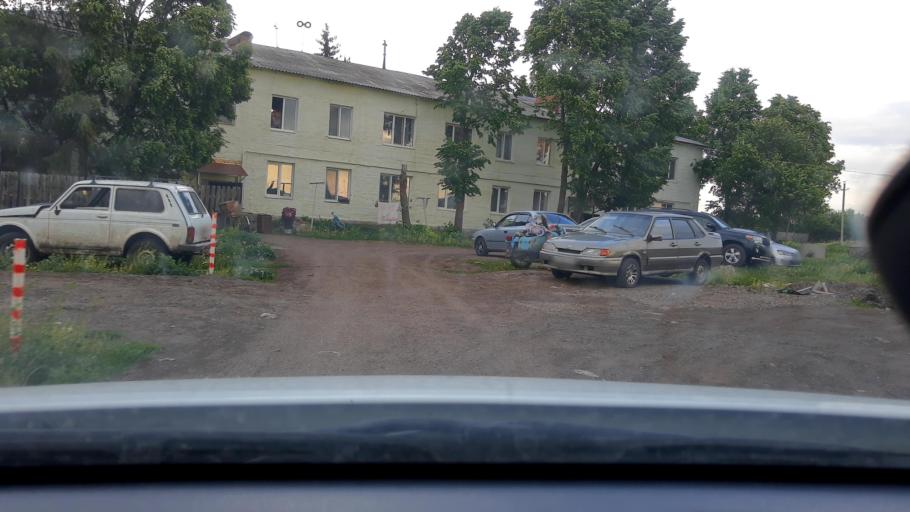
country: RU
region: Bashkortostan
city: Asanovo
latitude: 54.8896
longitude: 55.6275
